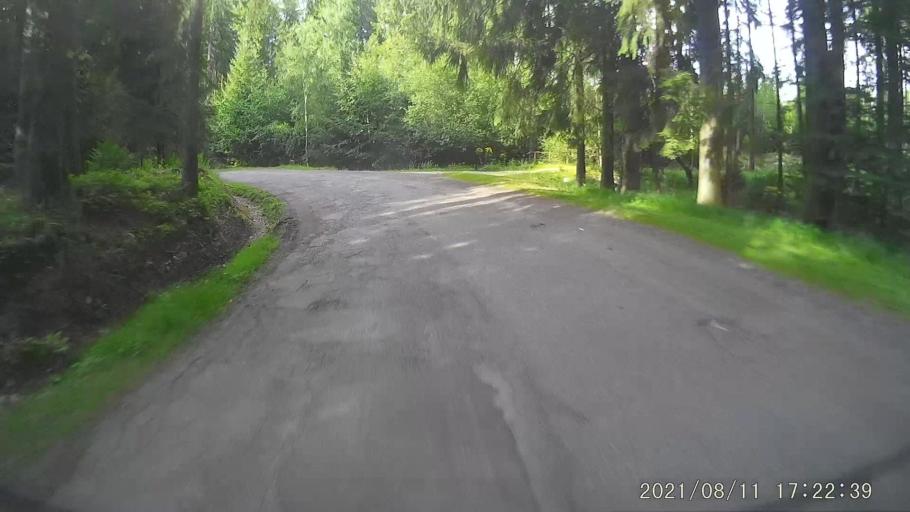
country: PL
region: Lower Silesian Voivodeship
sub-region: Powiat klodzki
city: Polanica-Zdroj
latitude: 50.3065
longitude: 16.5058
